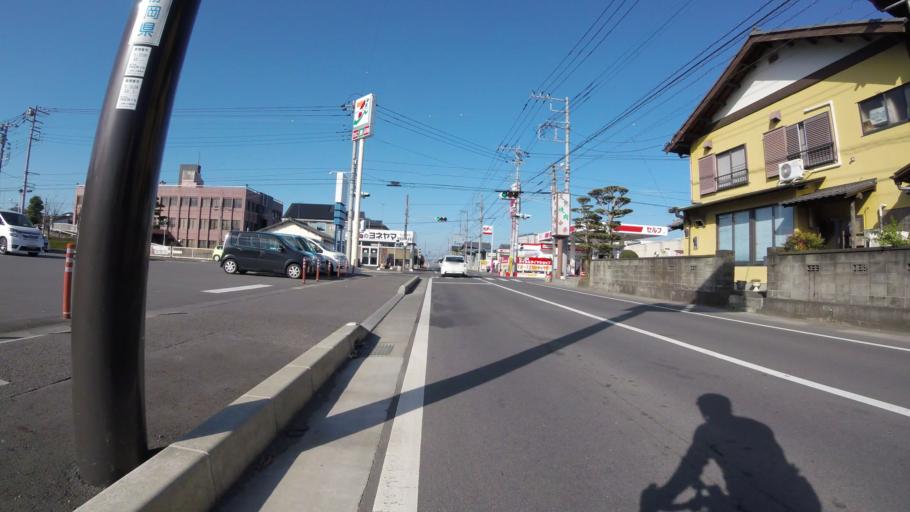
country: JP
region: Shizuoka
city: Mishima
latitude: 35.0585
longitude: 138.9537
